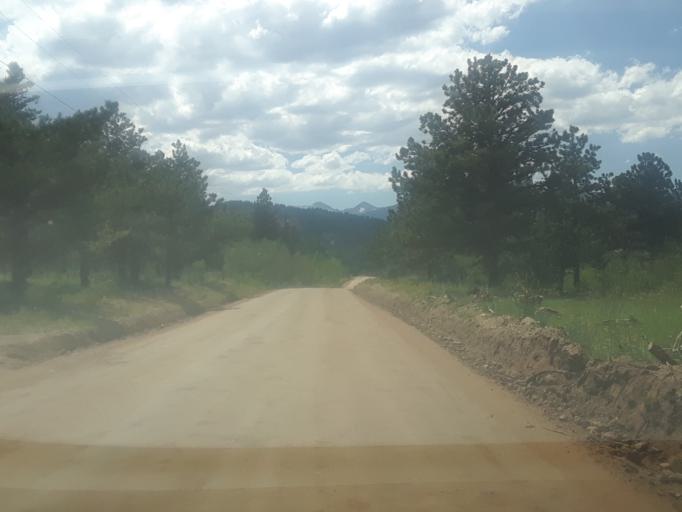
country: US
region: Colorado
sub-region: Boulder County
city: Nederland
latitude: 40.0550
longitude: -105.4479
